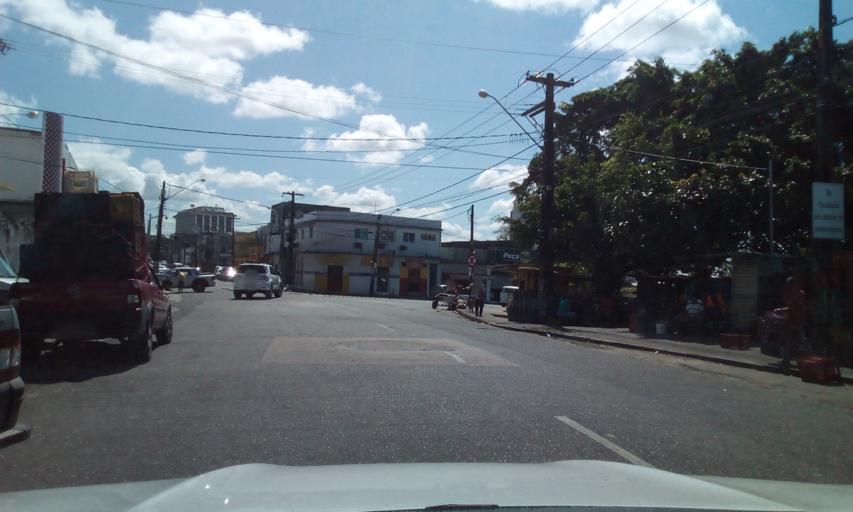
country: BR
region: Paraiba
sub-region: Joao Pessoa
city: Joao Pessoa
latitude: -7.1241
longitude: -34.8803
